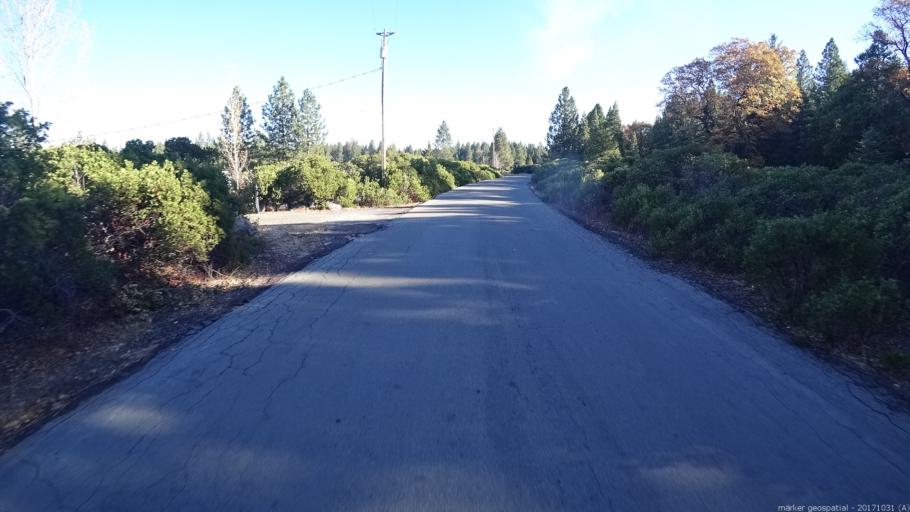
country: US
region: California
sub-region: Shasta County
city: Shingletown
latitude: 40.5215
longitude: -121.8395
